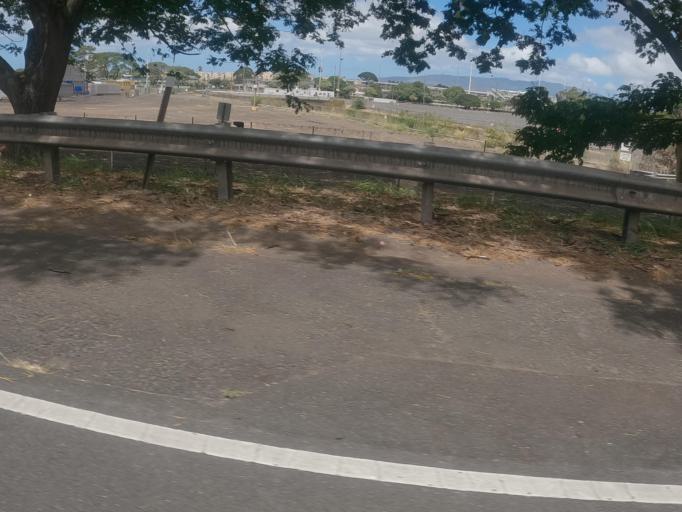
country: US
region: Hawaii
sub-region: Honolulu County
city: Halawa
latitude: 21.3695
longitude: -157.9274
